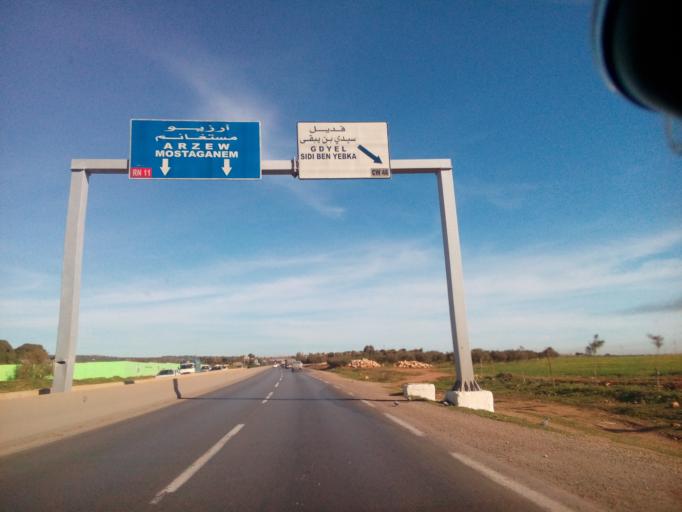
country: DZ
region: Oran
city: Ain el Bya
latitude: 35.7805
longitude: -0.4134
